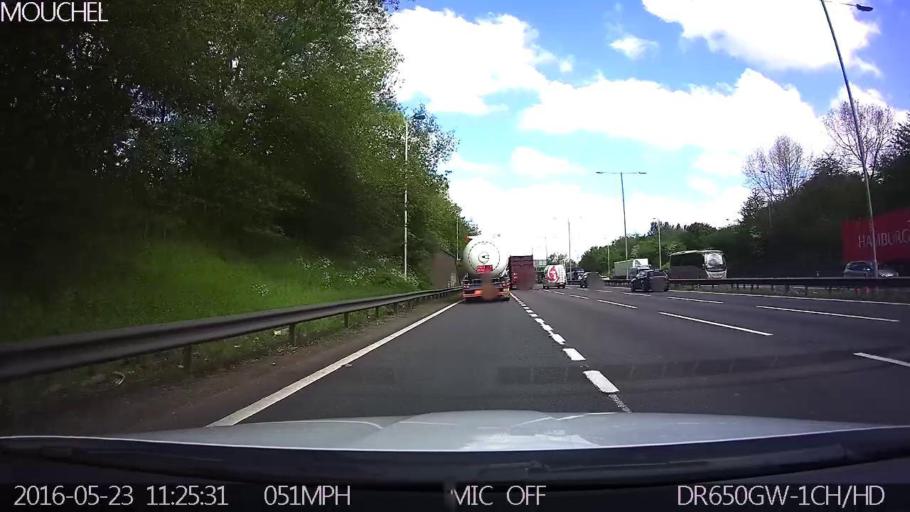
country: GB
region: England
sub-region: Walsall
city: Bloxwich
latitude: 52.5930
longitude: -2.0149
